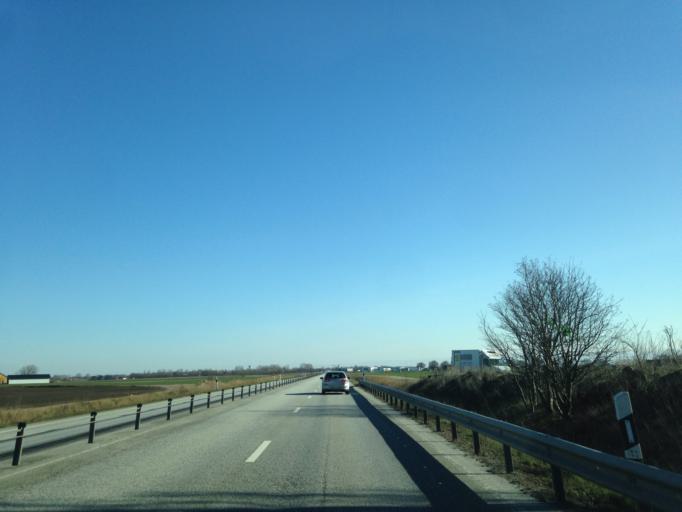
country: SE
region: Skane
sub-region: Vellinge Kommun
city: Vellinge
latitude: 55.4504
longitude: 13.0016
